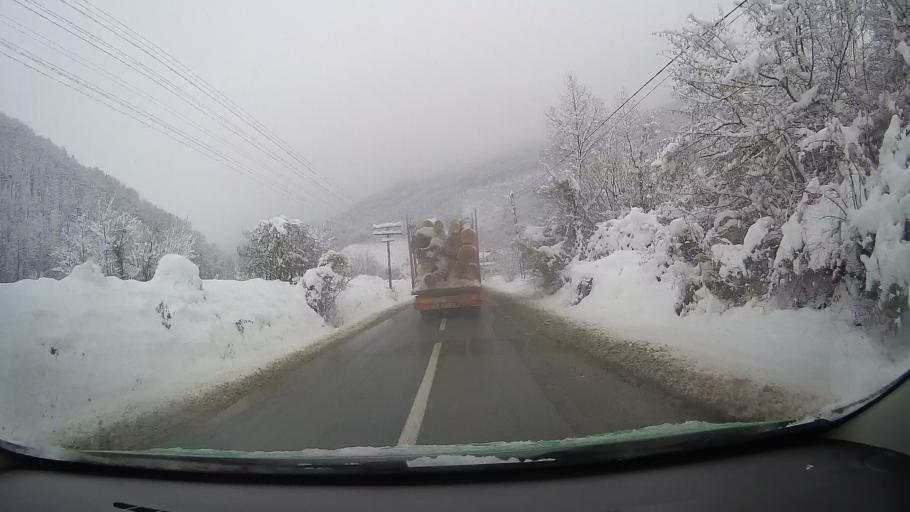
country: RO
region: Sibiu
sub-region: Comuna Orlat
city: Orlat
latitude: 45.7631
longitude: 23.9408
